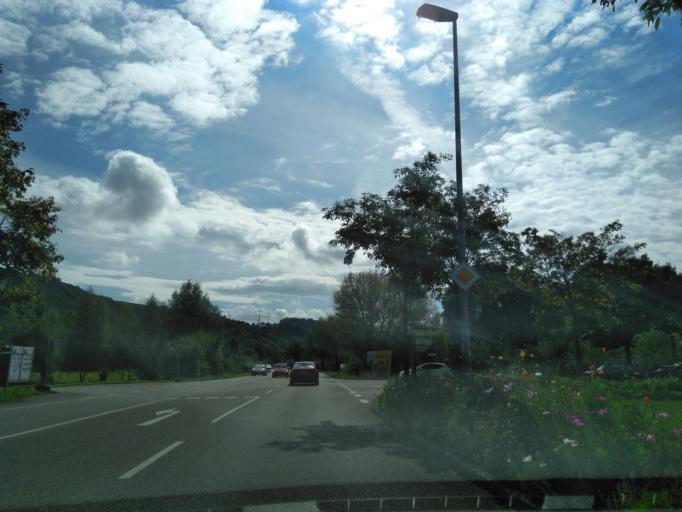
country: DE
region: Baden-Wuerttemberg
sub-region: Regierungsbezirk Stuttgart
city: Besigheim
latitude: 48.9933
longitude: 9.1450
